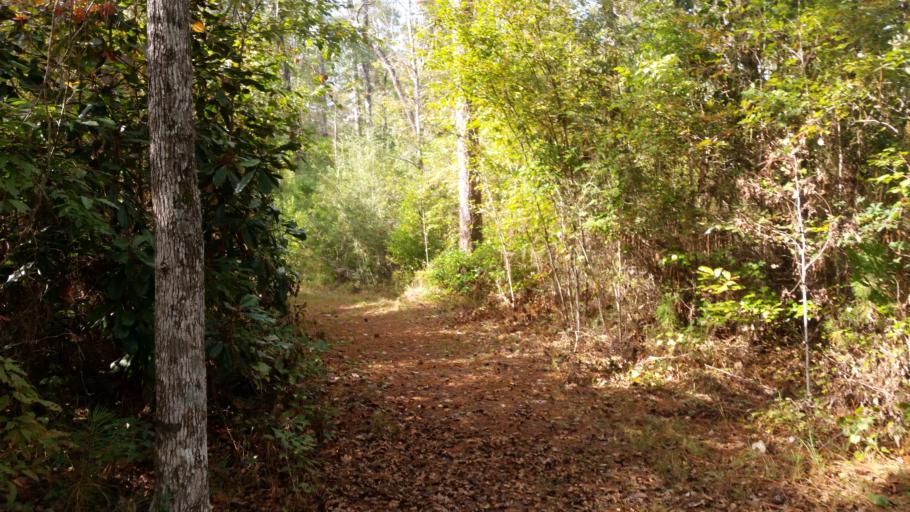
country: US
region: Mississippi
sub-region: Stone County
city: Wiggins
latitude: 30.9891
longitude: -89.0533
